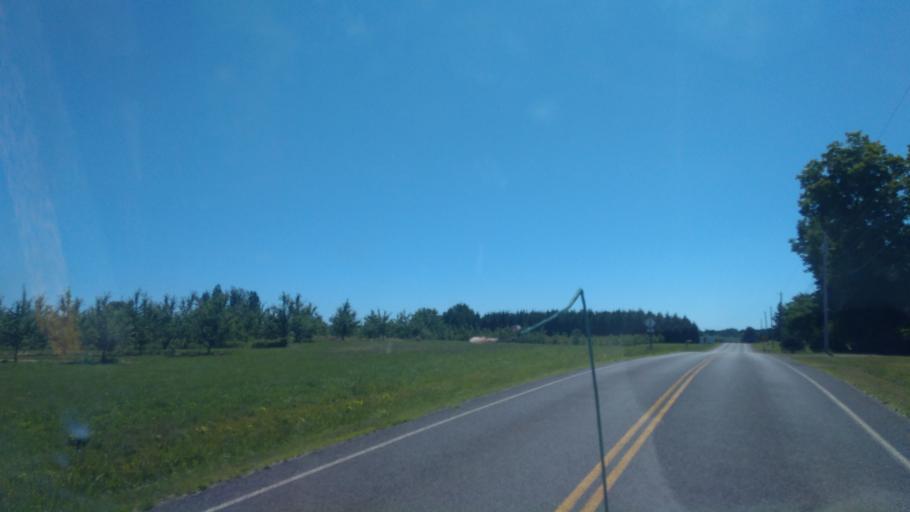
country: US
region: New York
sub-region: Wayne County
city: Sodus
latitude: 43.2770
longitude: -77.1182
